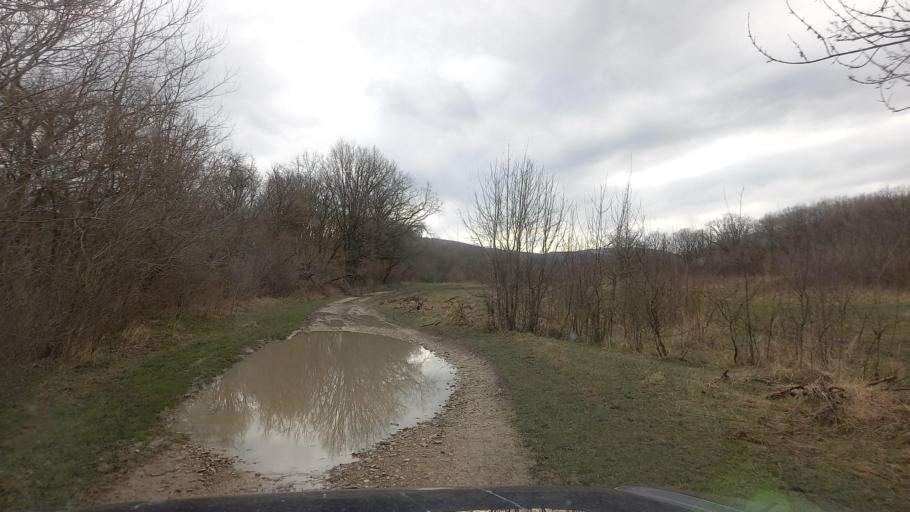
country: RU
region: Krasnodarskiy
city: Novorossiysk
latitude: 44.8562
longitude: 37.8443
